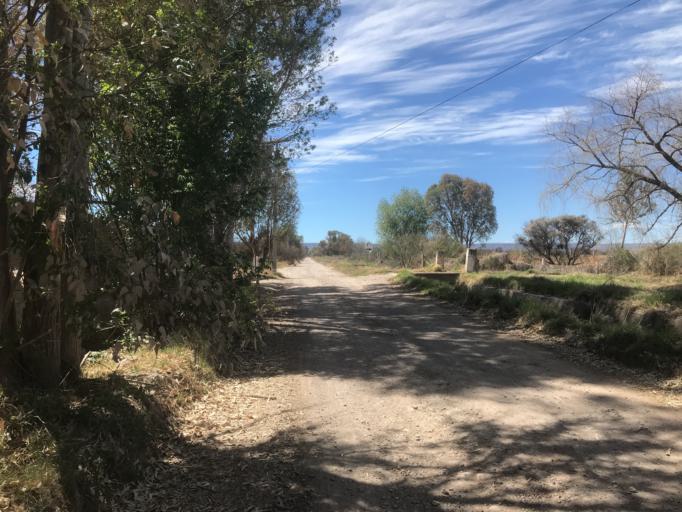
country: MX
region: Durango
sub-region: Durango
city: Sebastian Lerdo de Tejada
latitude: 23.9829
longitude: -104.6222
